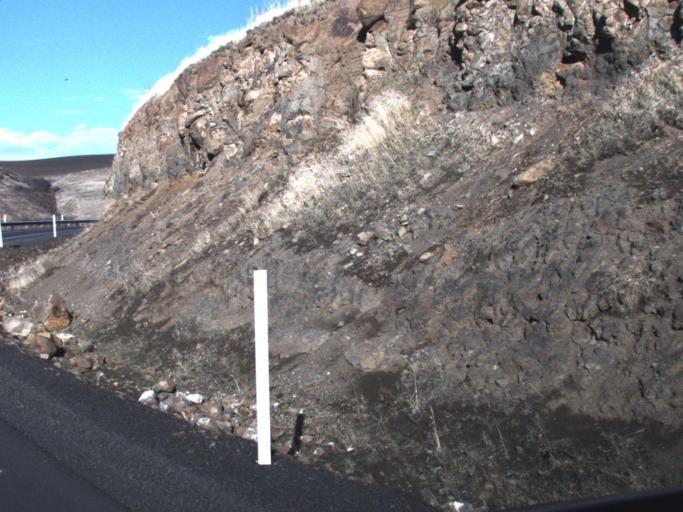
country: US
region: Washington
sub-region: Whitman County
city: Colfax
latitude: 46.7183
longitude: -117.4833
